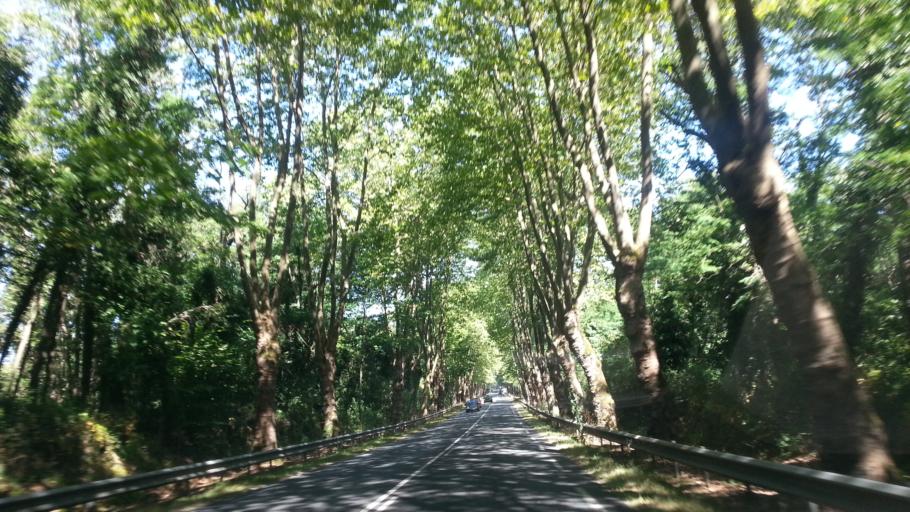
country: FR
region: Aquitaine
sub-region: Departement de la Gironde
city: Martillac
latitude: 44.7060
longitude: -0.5155
